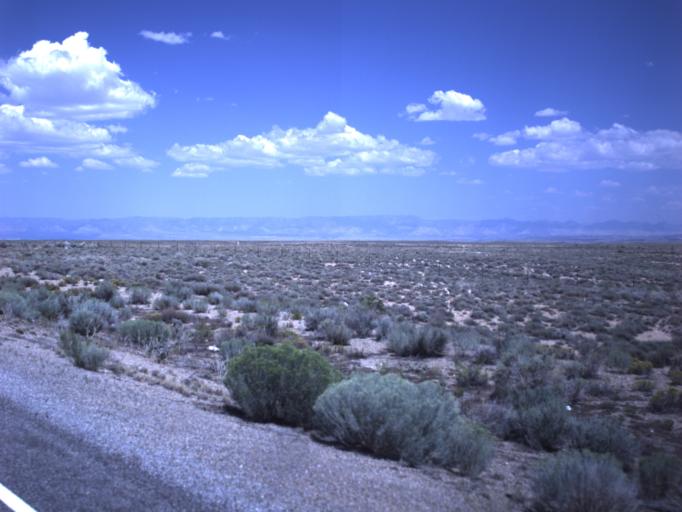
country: US
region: Utah
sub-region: Emery County
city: Huntington
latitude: 39.4002
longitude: -110.8910
